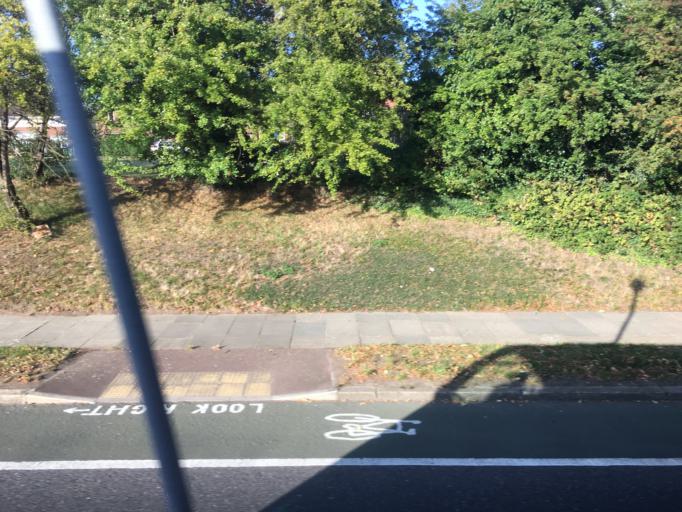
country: GB
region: England
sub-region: Greater London
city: Blackheath
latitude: 51.4639
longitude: 0.0358
